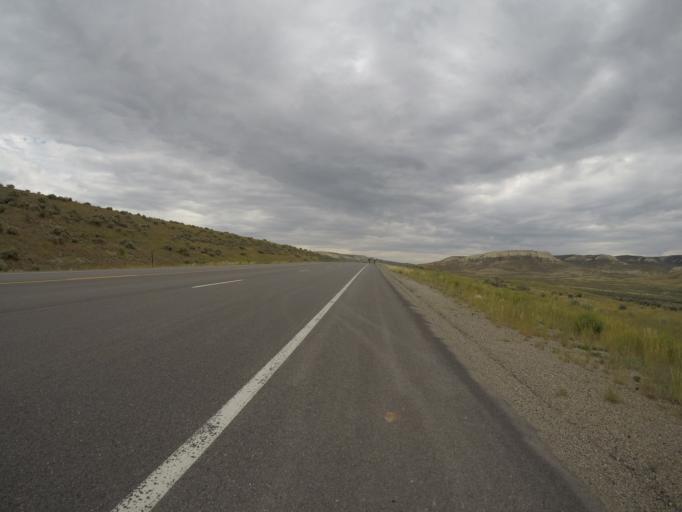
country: US
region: Wyoming
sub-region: Lincoln County
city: Kemmerer
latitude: 41.8109
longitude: -110.6803
